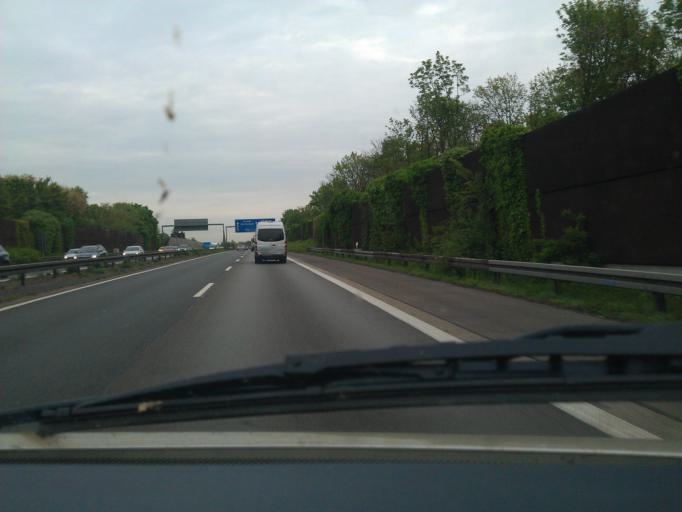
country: DE
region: North Rhine-Westphalia
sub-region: Regierungsbezirk Dusseldorf
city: Krefeld
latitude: 51.3308
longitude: 6.6283
